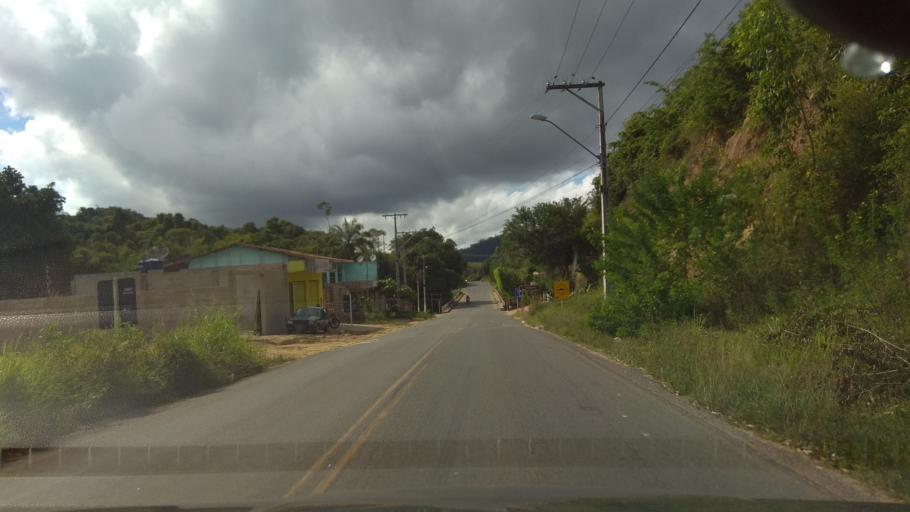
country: BR
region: Bahia
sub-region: Ubaira
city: Ubaira
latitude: -13.2550
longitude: -39.5854
